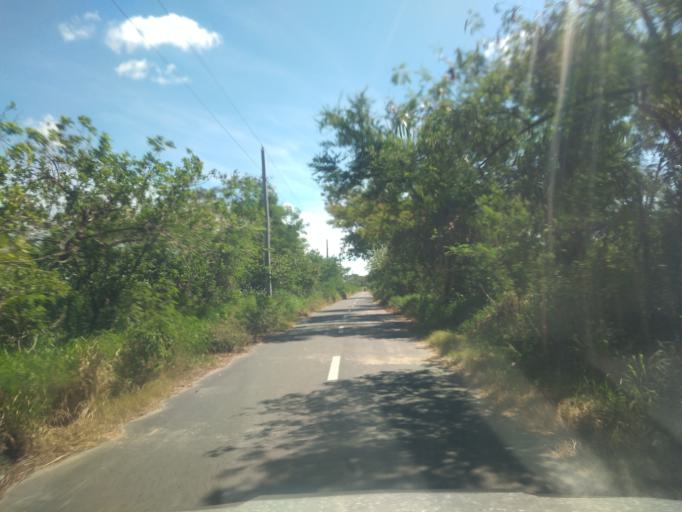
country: PH
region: Central Luzon
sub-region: Province of Pampanga
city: Balas
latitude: 15.0506
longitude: 120.5854
